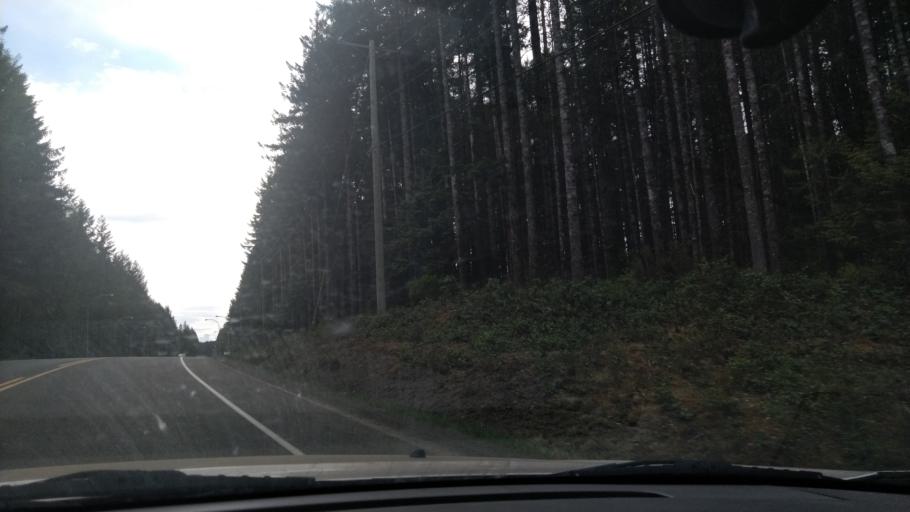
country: CA
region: British Columbia
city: Campbell River
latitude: 50.0204
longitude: -125.3533
